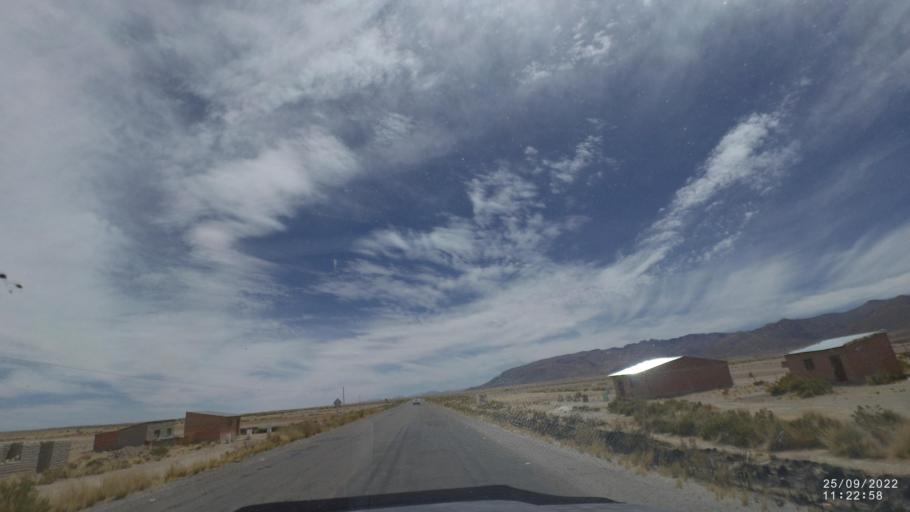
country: BO
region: Oruro
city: Challapata
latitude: -19.1175
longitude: -66.7697
